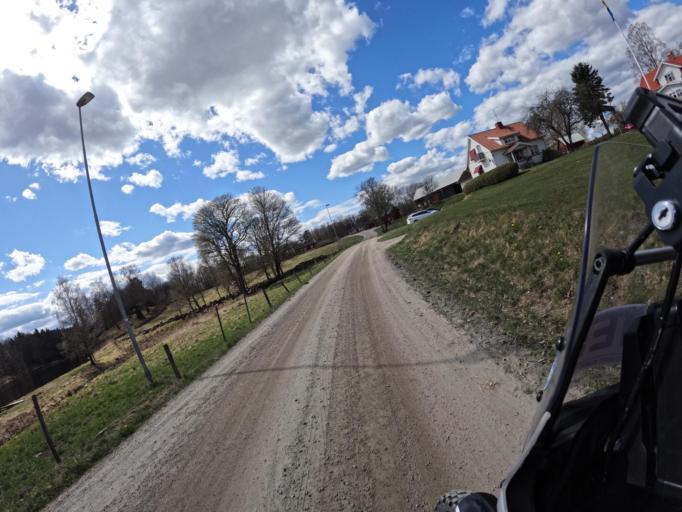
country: SE
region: Vaestra Goetaland
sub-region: Ulricehamns Kommun
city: Ulricehamn
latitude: 57.9450
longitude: 13.3057
